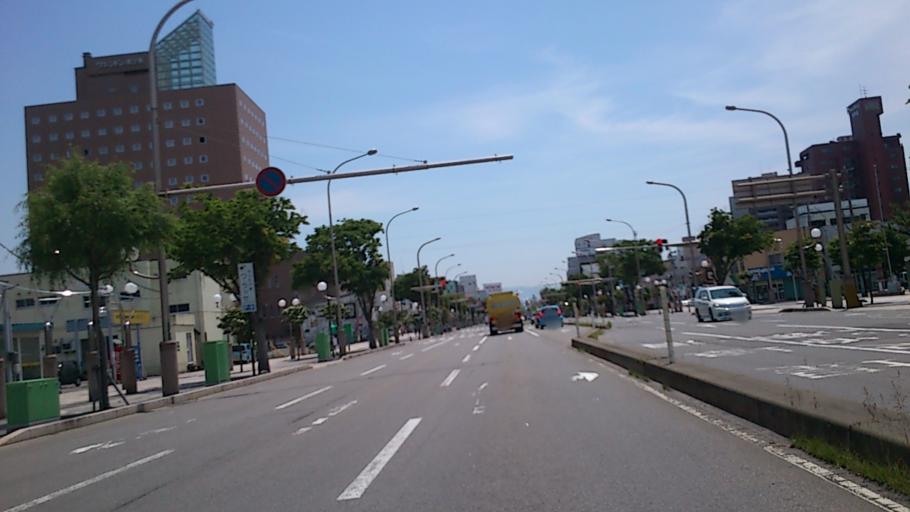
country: JP
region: Aomori
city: Aomori Shi
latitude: 40.8286
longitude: 140.7457
